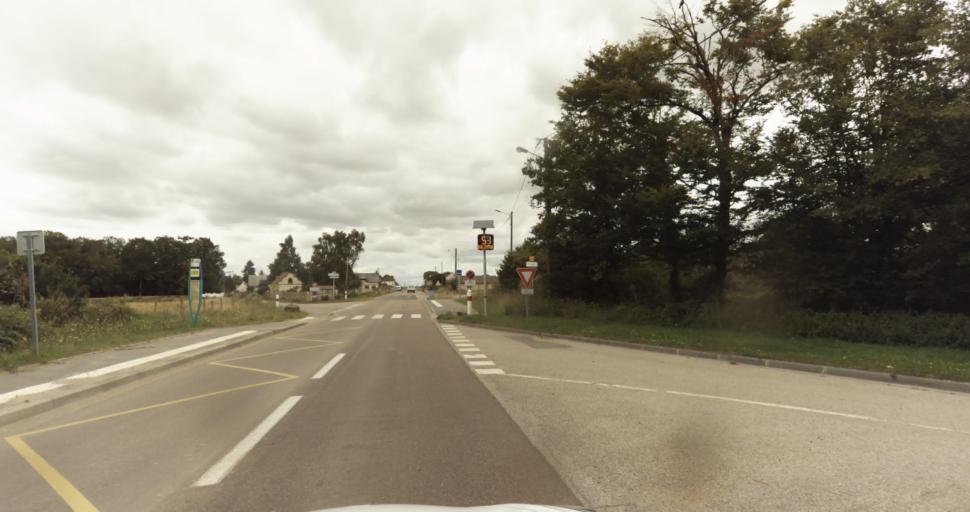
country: FR
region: Haute-Normandie
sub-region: Departement de l'Eure
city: La Madeleine-de-Nonancourt
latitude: 48.8210
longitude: 1.1862
